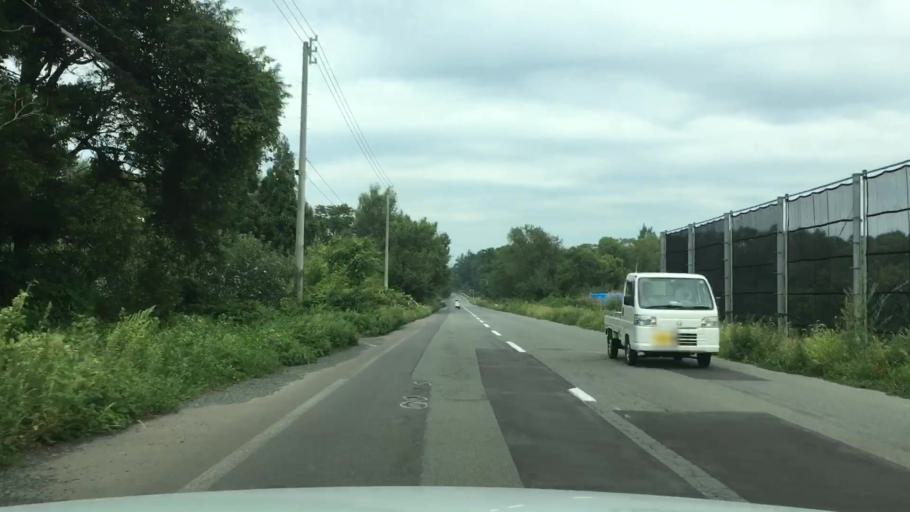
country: JP
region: Aomori
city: Hirosaki
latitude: 40.6815
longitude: 140.3710
